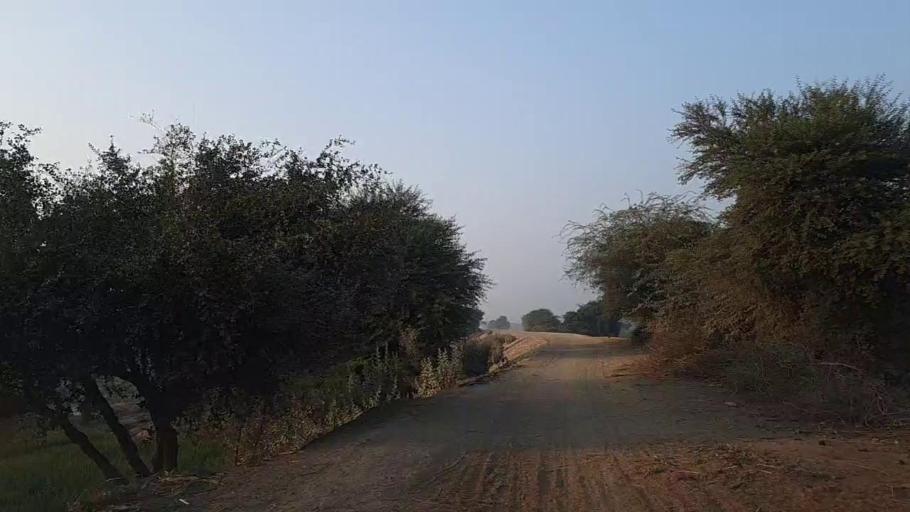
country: PK
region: Sindh
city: Sann
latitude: 26.1794
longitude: 68.0956
